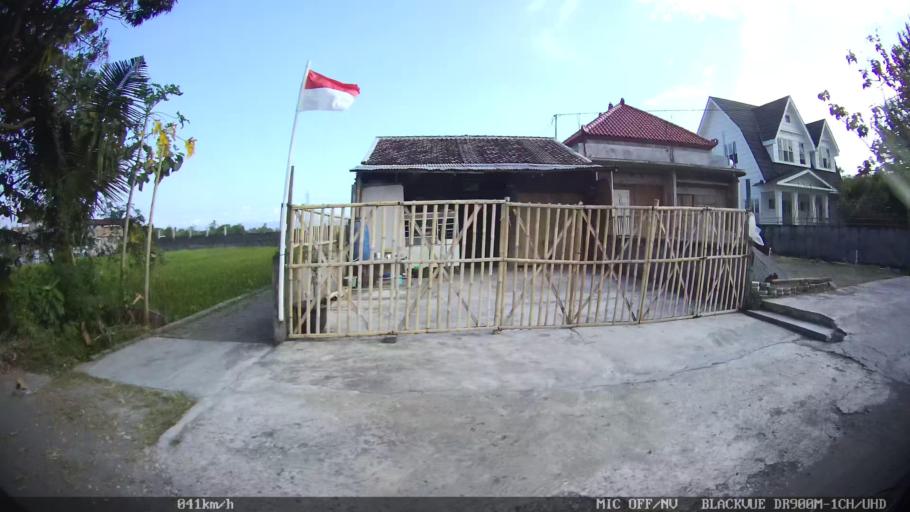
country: ID
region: Daerah Istimewa Yogyakarta
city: Sewon
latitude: -7.8705
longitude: 110.3562
